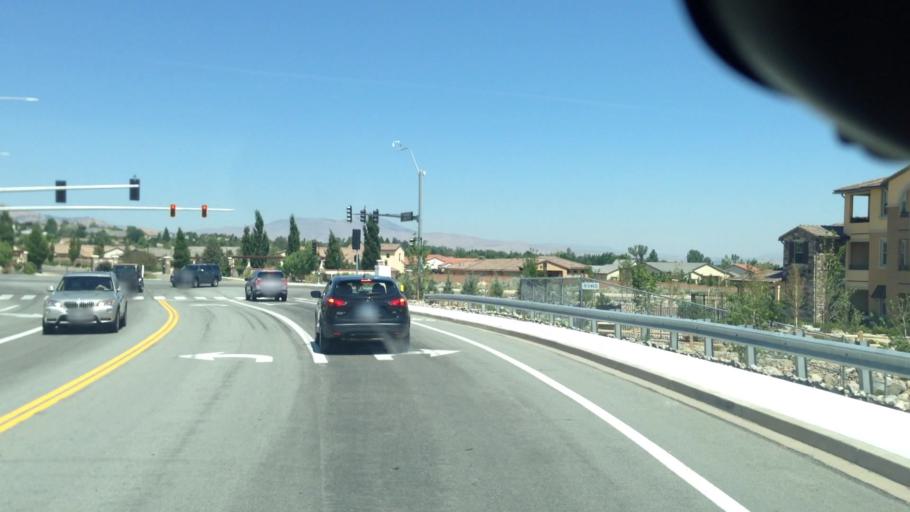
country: US
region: Nevada
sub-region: Washoe County
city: Sparks
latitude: 39.4081
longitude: -119.7602
